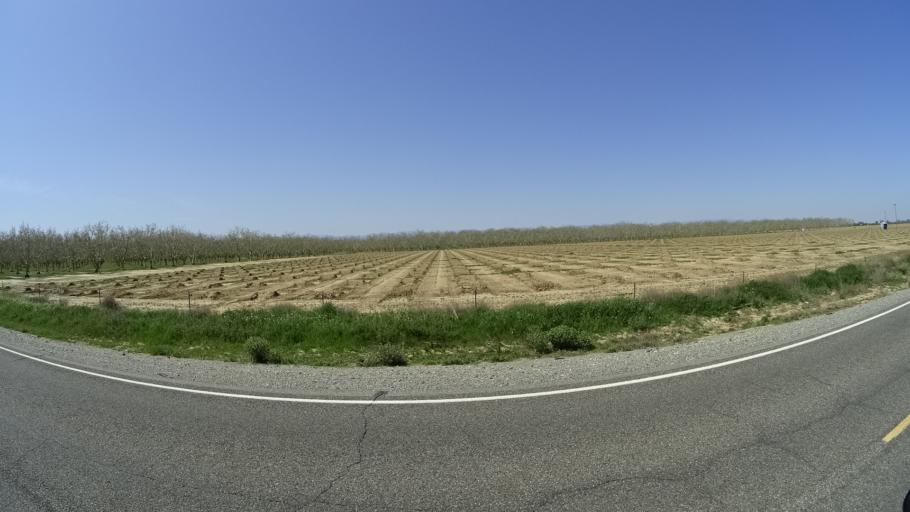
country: US
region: California
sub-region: Glenn County
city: Orland
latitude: 39.6430
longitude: -122.1972
